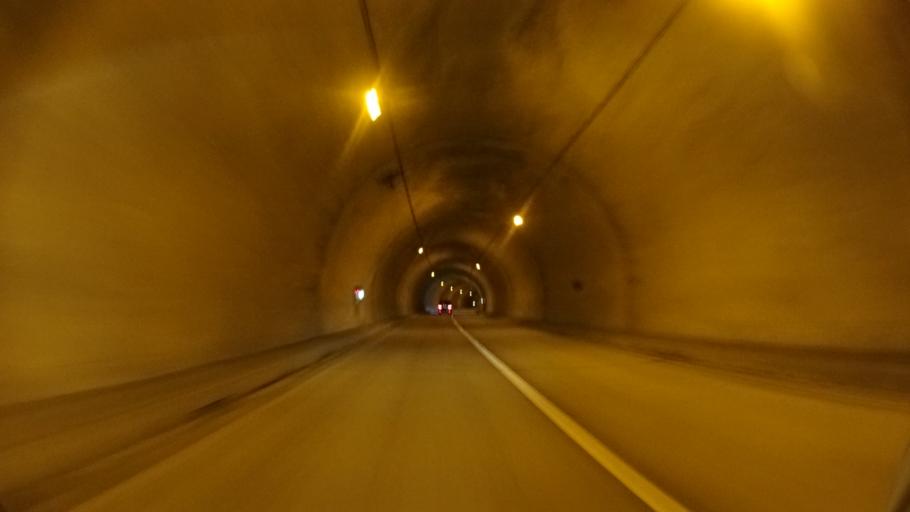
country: JP
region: Tokushima
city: Ikedacho
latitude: 33.8610
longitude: 133.9009
